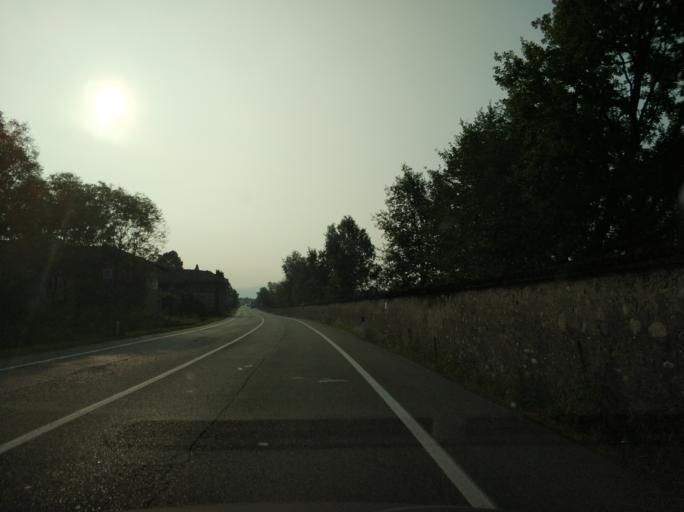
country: IT
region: Piedmont
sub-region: Provincia di Torino
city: Venaria Reale
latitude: 45.1557
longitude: 7.6132
